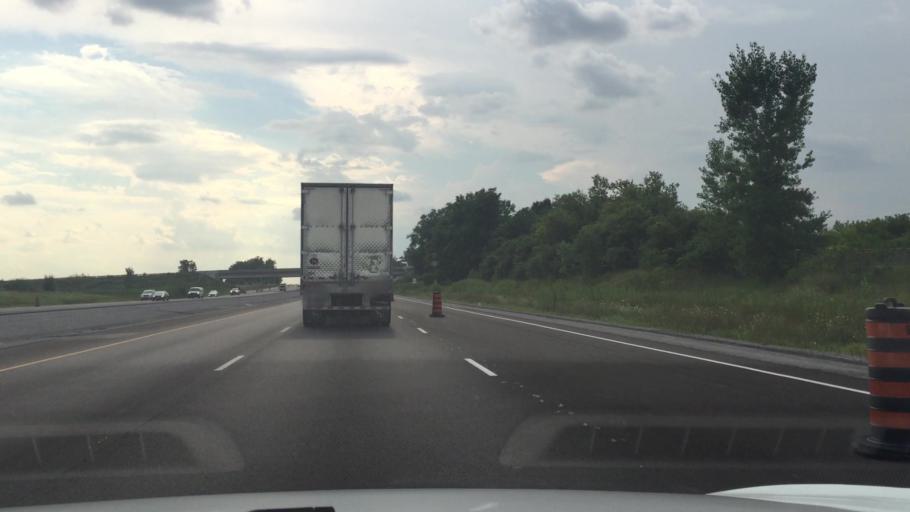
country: CA
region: Ontario
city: Pickering
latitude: 43.9098
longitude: -79.1299
